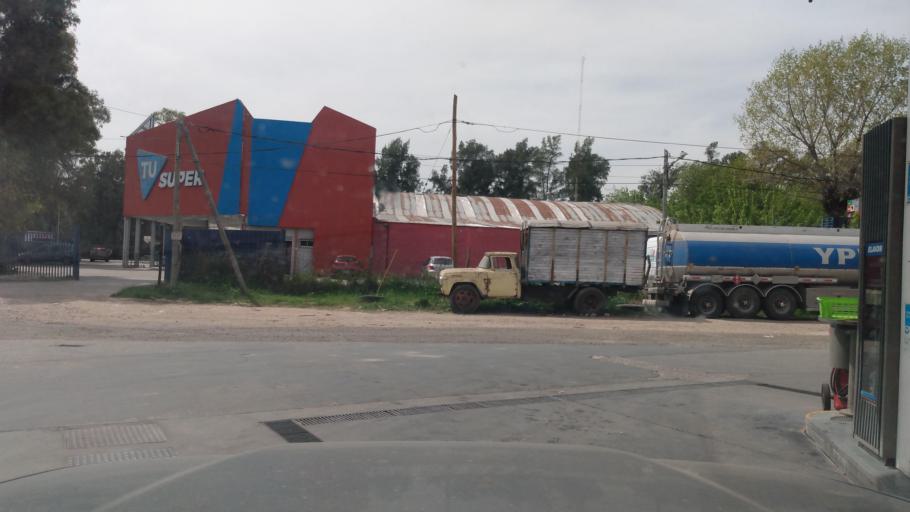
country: AR
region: Buenos Aires
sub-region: Partido de Pilar
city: Pilar
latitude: -34.4467
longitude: -58.9032
